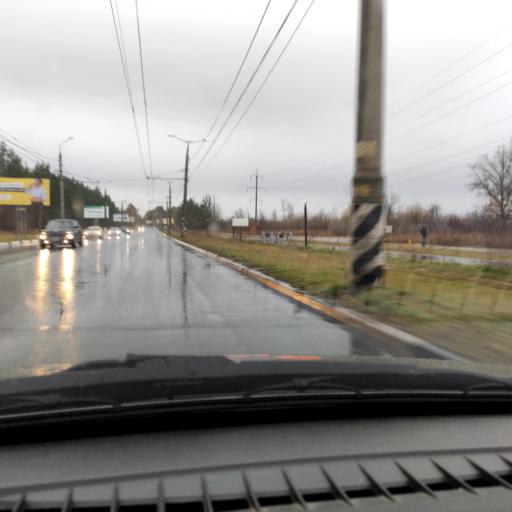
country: RU
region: Samara
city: Tol'yatti
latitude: 53.4976
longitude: 49.3881
